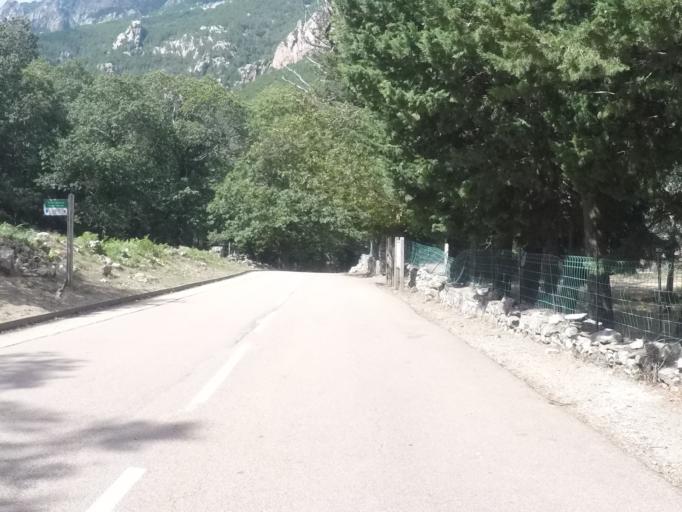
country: FR
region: Corsica
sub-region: Departement de la Corse-du-Sud
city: Zonza
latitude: 41.8102
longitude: 9.2465
